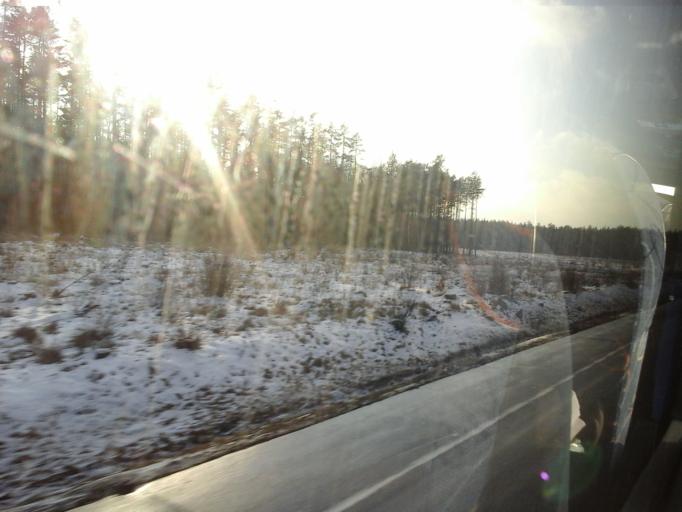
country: PL
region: Warmian-Masurian Voivodeship
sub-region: Powiat olsztynski
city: Olsztynek
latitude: 53.5839
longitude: 20.1876
